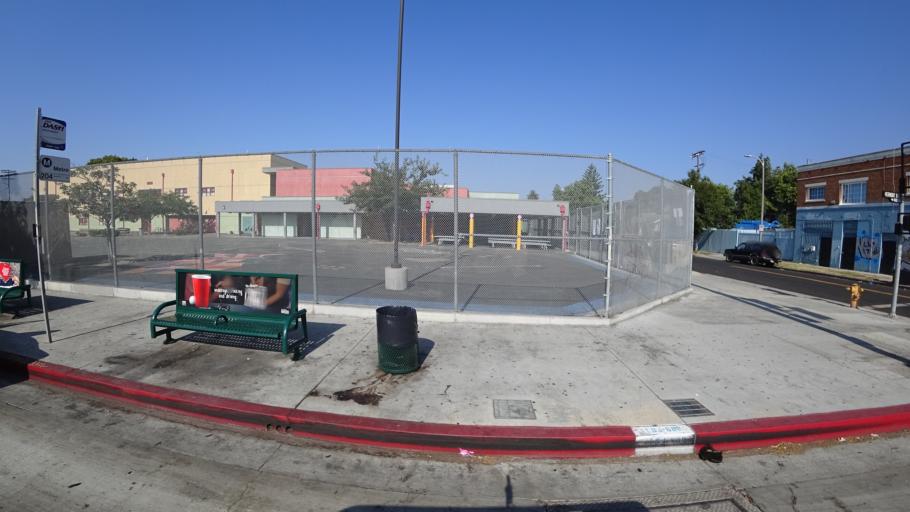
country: US
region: California
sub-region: Los Angeles County
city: View Park-Windsor Hills
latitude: 34.0016
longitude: -118.2916
